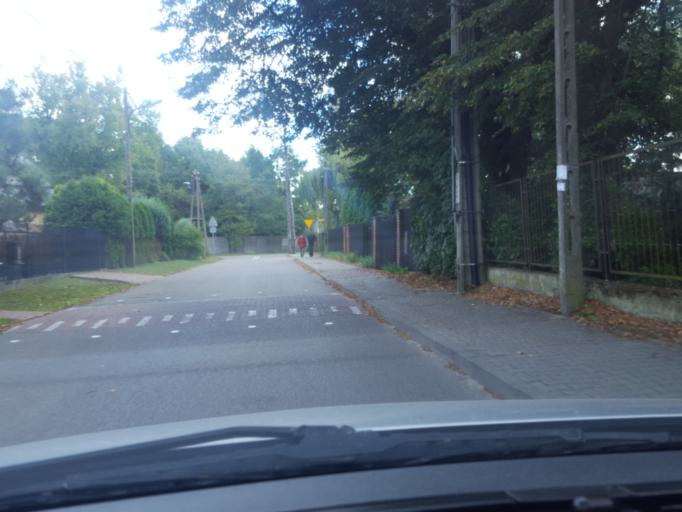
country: PL
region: Masovian Voivodeship
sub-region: Warszawa
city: Rembertow
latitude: 52.2684
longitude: 21.1693
